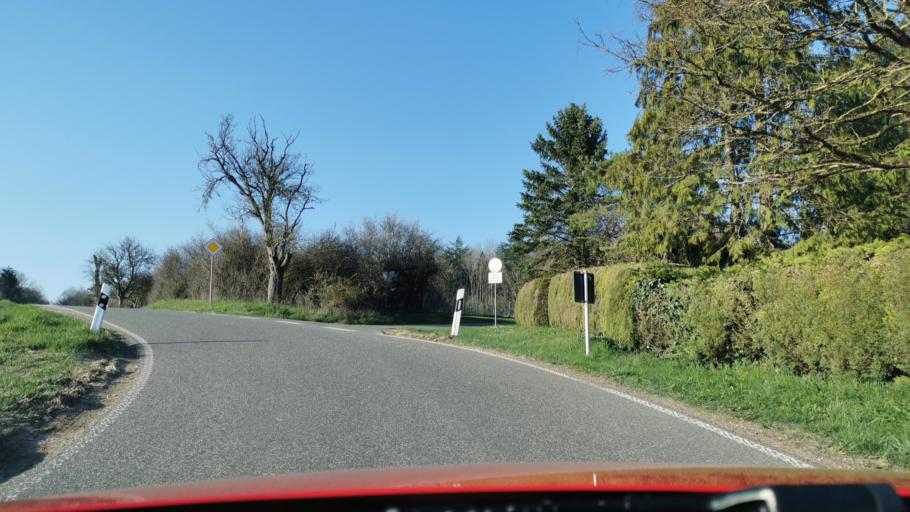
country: DE
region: Rheinland-Pfalz
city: Trierweiler
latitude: 49.7639
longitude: 6.5549
